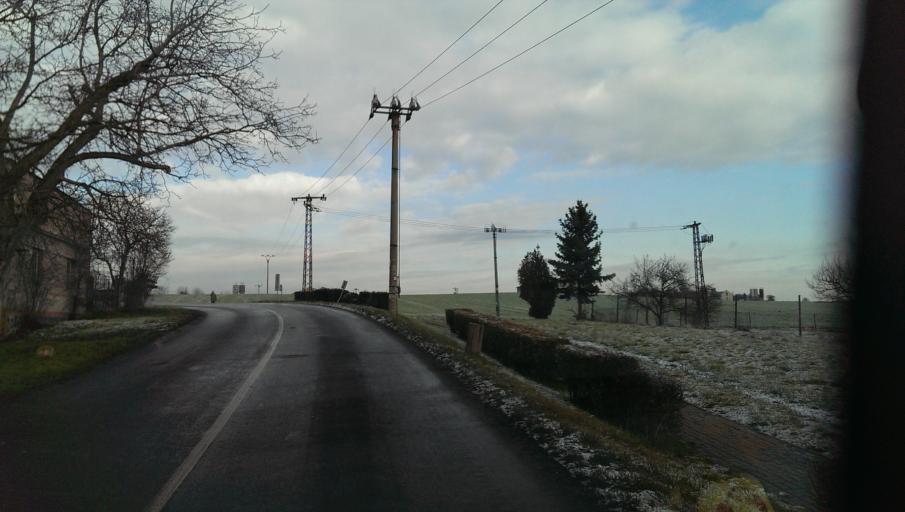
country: CZ
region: Ustecky
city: Libochovice
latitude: 50.4087
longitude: 14.0380
